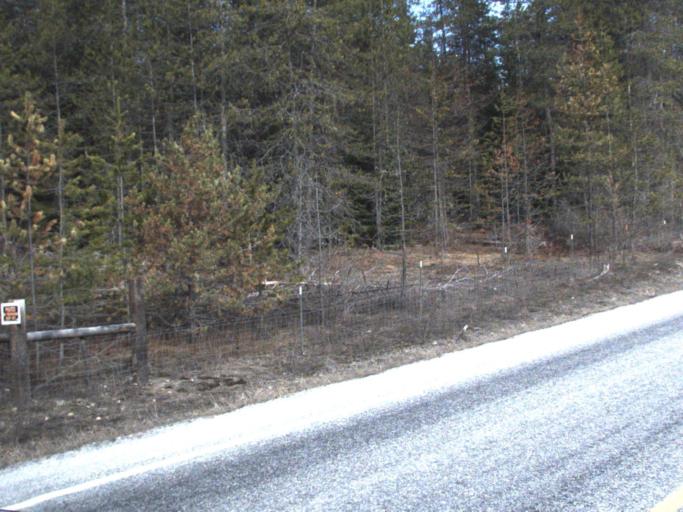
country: US
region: Washington
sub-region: Stevens County
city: Chewelah
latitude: 48.6291
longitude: -117.3686
